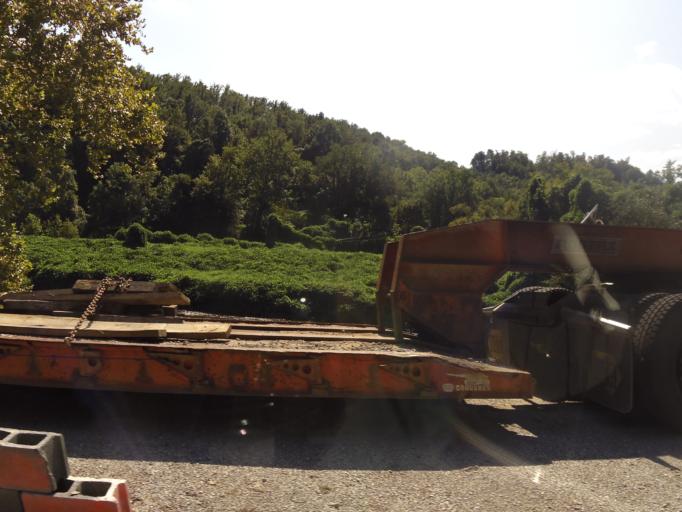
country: US
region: Kentucky
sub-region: Harlan County
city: Harlan
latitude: 36.8575
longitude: -83.3205
